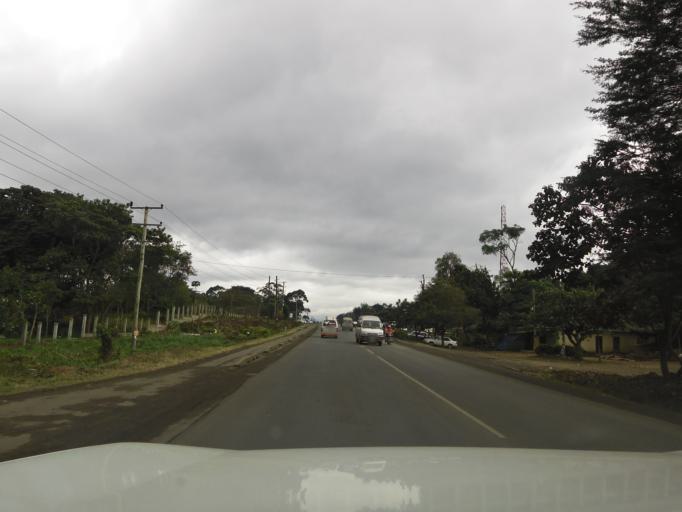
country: TZ
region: Arusha
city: Arusha
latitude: -3.3651
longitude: 36.7061
